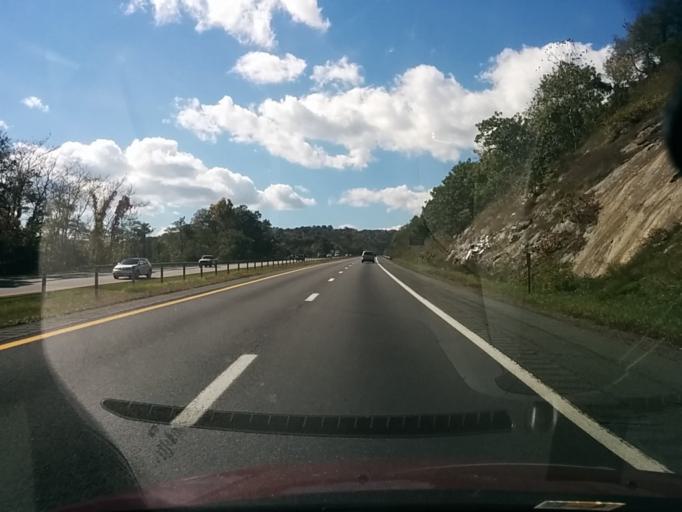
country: US
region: Virginia
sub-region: City of Waynesboro
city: Waynesboro
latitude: 38.0347
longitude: -78.8481
